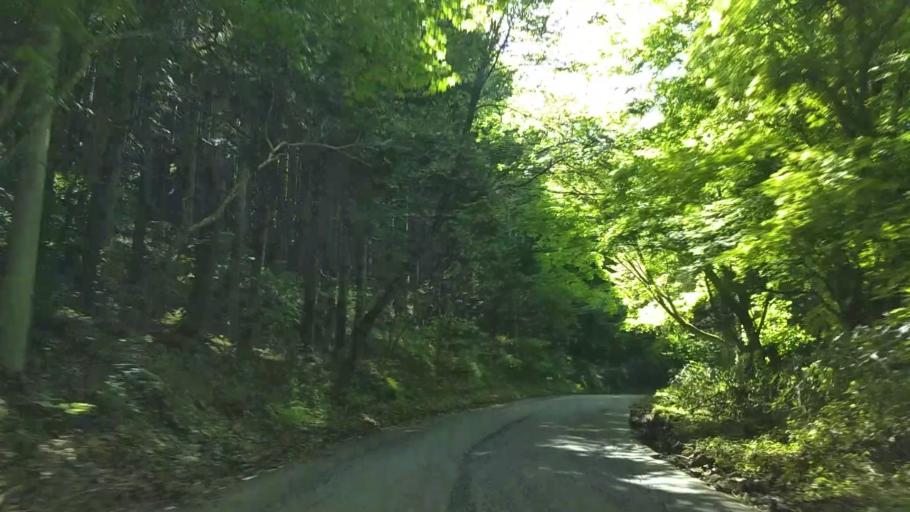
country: JP
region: Shizuoka
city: Gotemba
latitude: 35.2847
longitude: 138.9695
